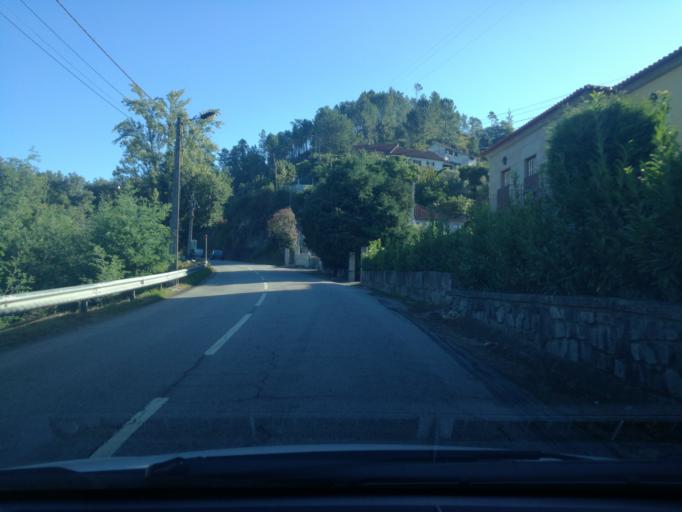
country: PT
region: Braga
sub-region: Vieira do Minho
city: Real
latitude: 41.6821
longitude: -8.1728
